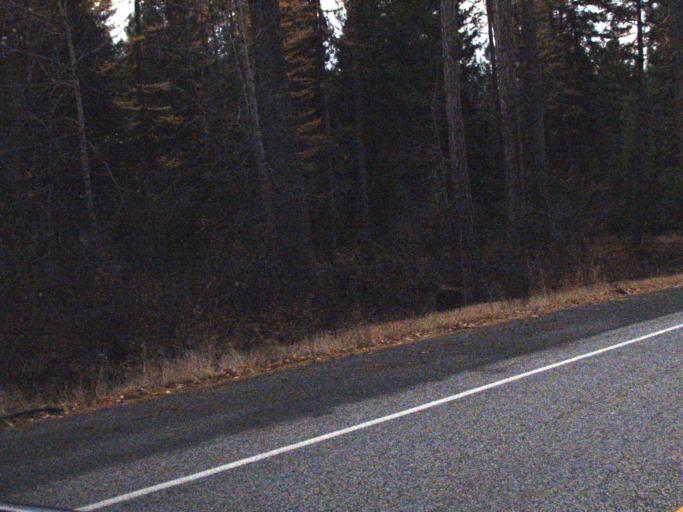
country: US
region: Washington
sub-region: Ferry County
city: Republic
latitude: 48.6015
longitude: -118.6541
